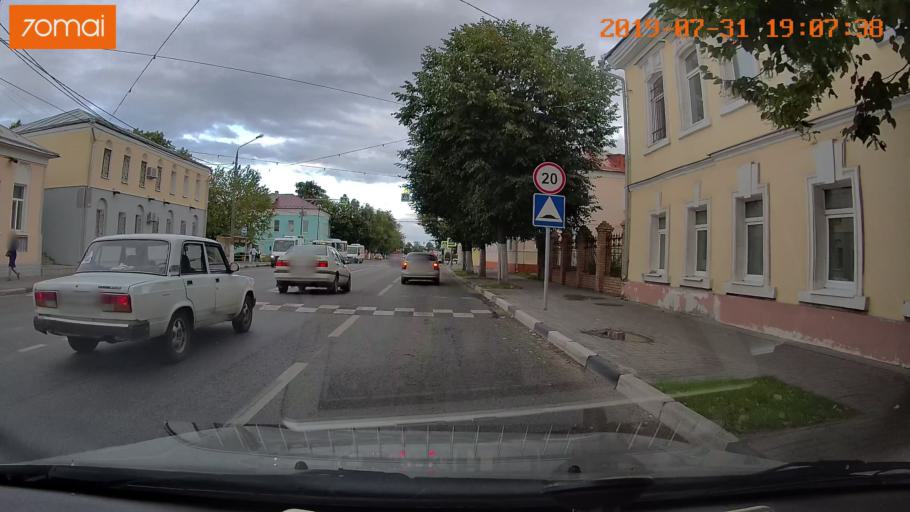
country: RU
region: Moskovskaya
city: Kolomna
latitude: 55.0978
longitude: 38.7614
